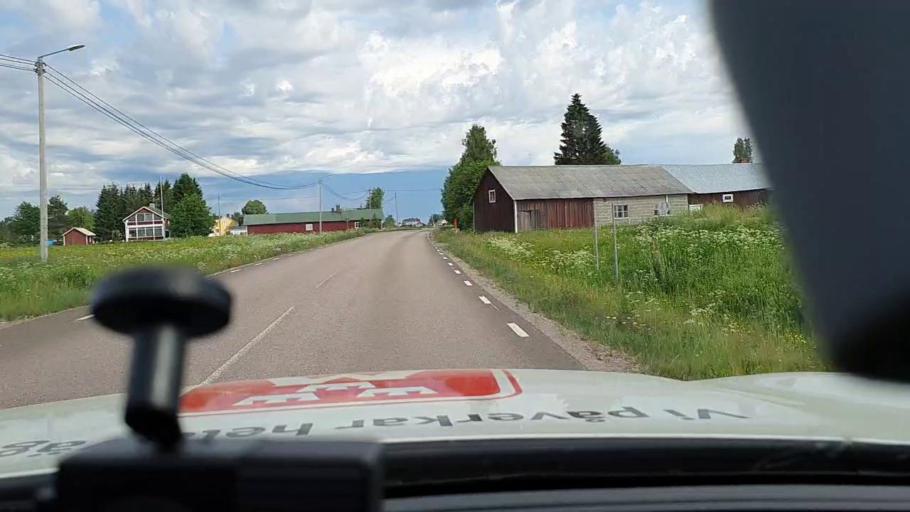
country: SE
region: Norrbotten
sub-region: Bodens Kommun
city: Saevast
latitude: 65.7023
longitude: 21.7695
